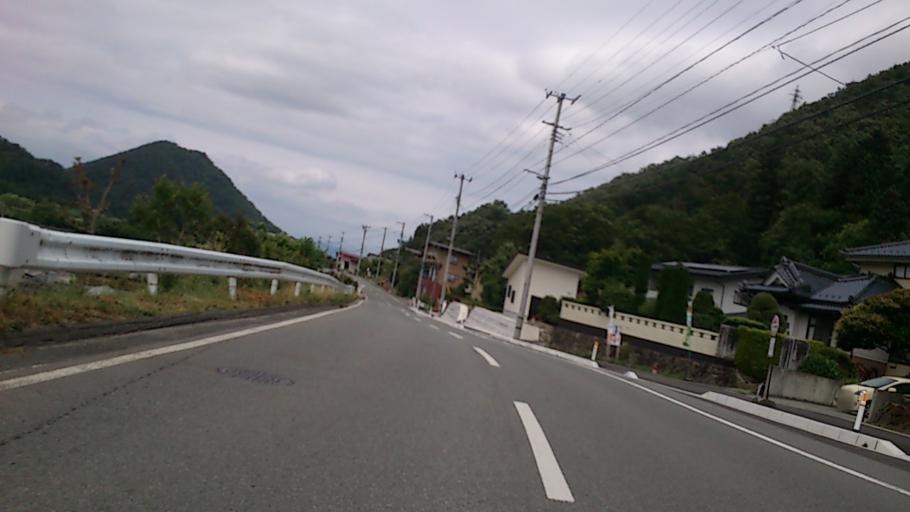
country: JP
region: Yamagata
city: Tendo
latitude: 38.3118
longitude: 140.4244
